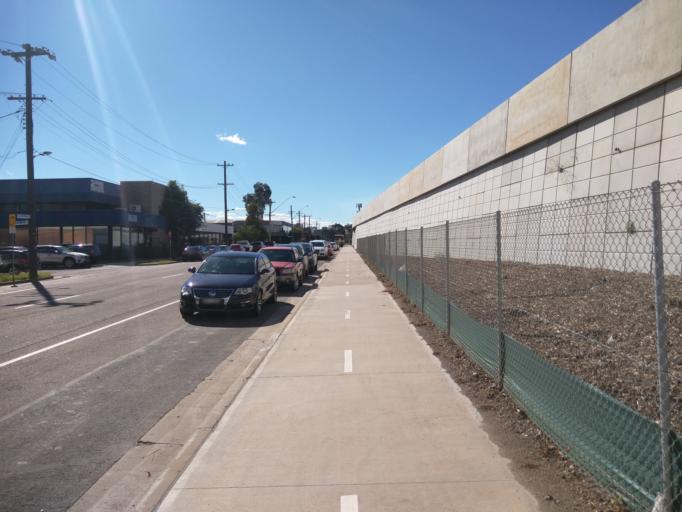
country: AU
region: New South Wales
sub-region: Parramatta
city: Granville
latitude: -33.8337
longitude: 151.0245
